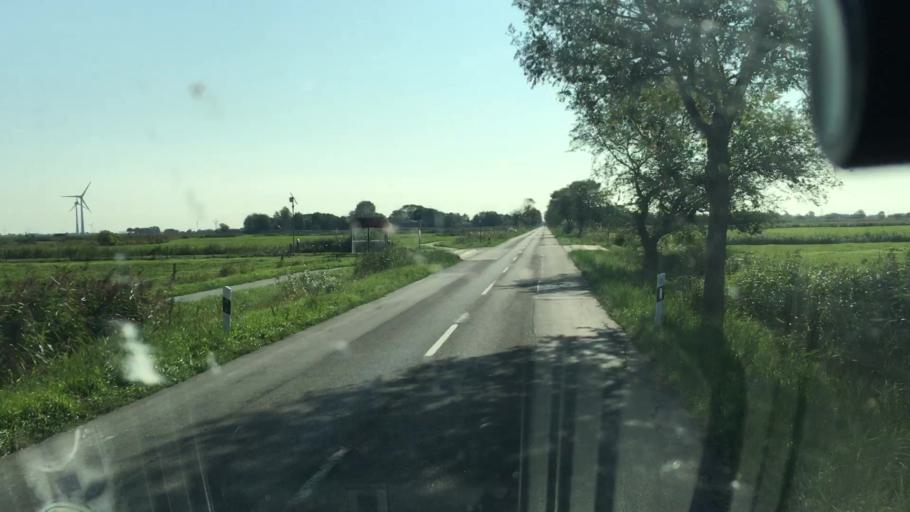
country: DE
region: Lower Saxony
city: Werdum
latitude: 53.6652
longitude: 7.6876
